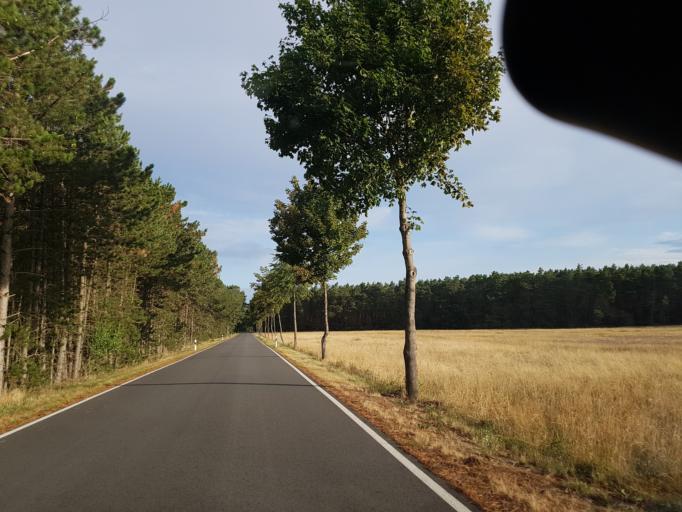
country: DE
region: Saxony-Anhalt
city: Holzdorf
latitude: 51.7910
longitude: 13.1061
